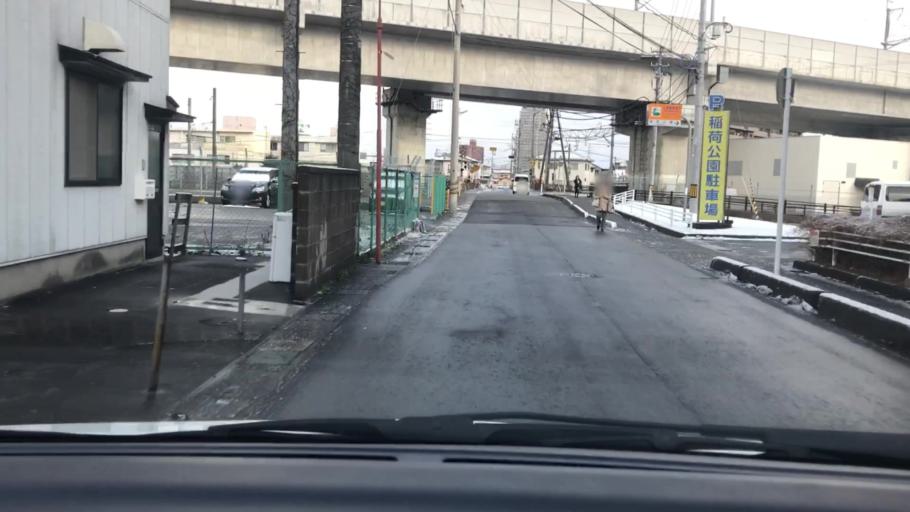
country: JP
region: Toyama
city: Toyama-shi
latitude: 36.6986
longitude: 137.2297
